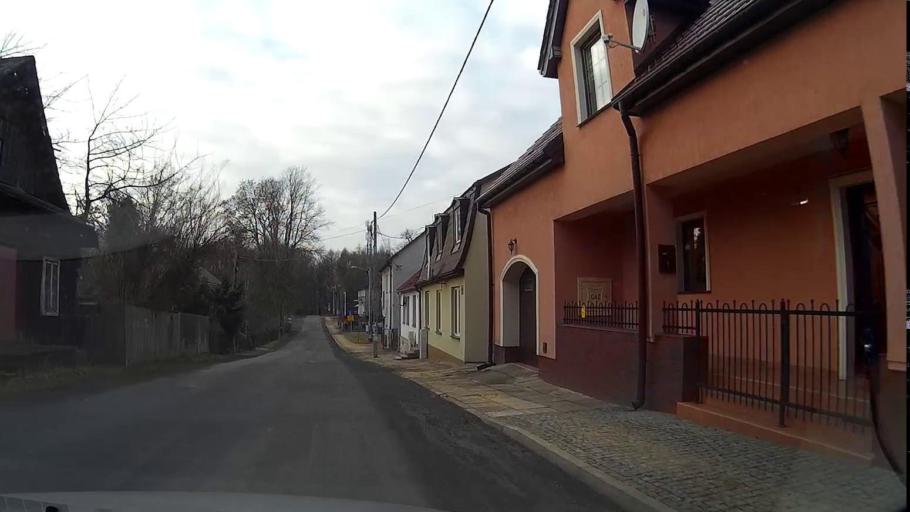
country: PL
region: Lesser Poland Voivodeship
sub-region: Powiat chrzanowski
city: Alwernia
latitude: 50.0692
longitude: 19.5384
